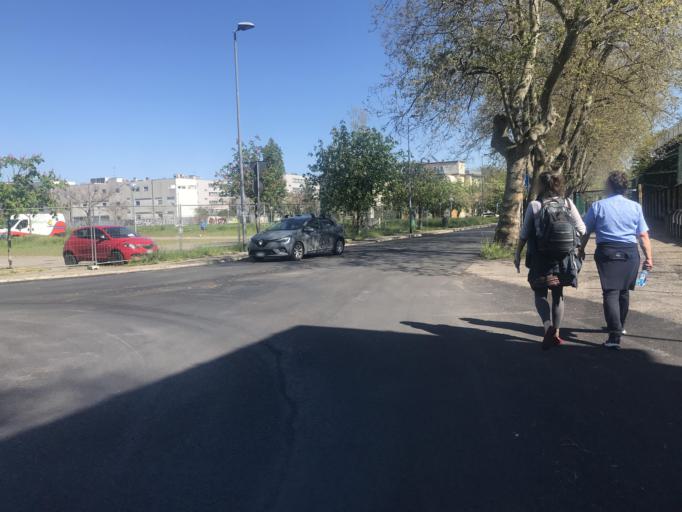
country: IT
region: Emilia-Romagna
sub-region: Provincia di Rimini
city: Rimini
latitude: 44.0542
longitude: 12.5776
